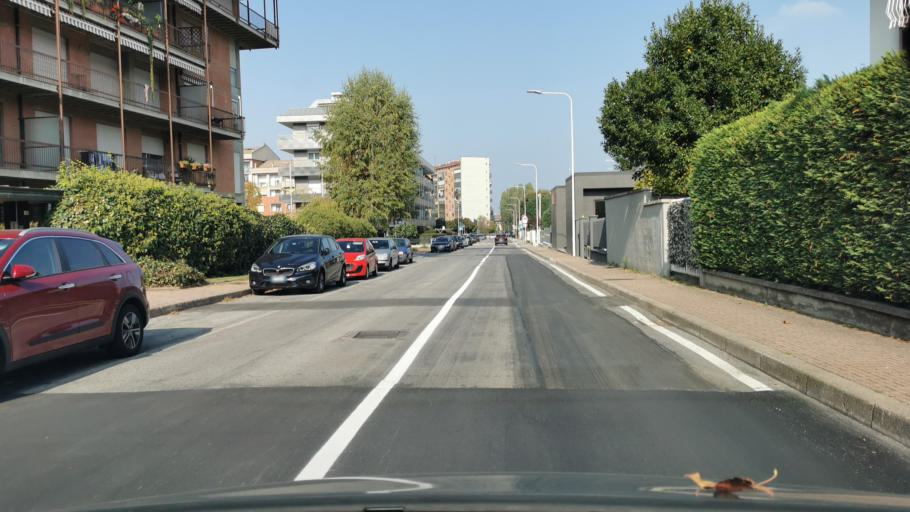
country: IT
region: Piedmont
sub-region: Provincia di Cuneo
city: Cuneo
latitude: 44.3721
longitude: 7.5391
